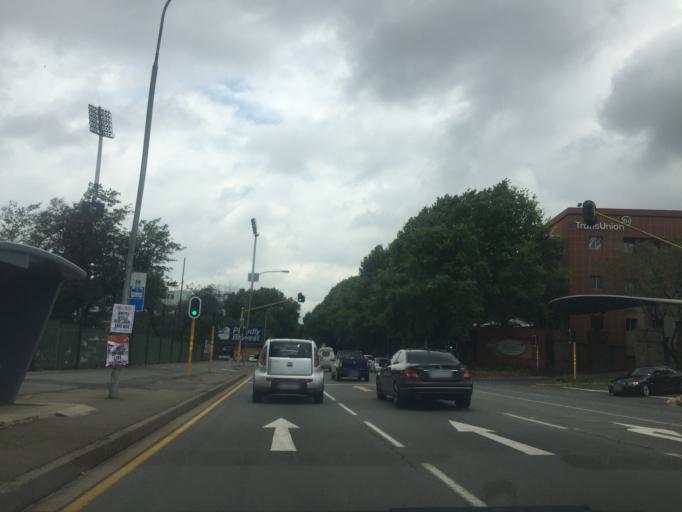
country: ZA
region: Gauteng
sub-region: City of Johannesburg Metropolitan Municipality
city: Johannesburg
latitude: -26.1332
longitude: 28.0556
